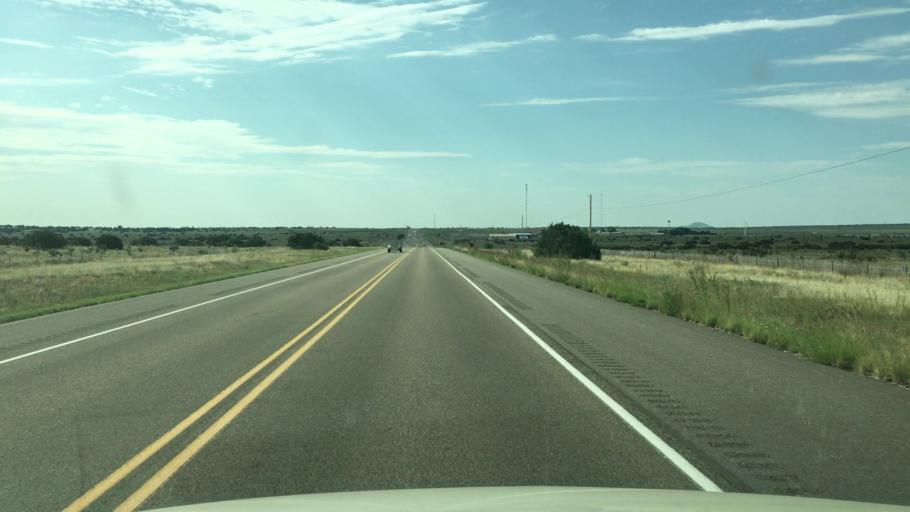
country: US
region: New Mexico
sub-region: Torrance County
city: Moriarty
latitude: 35.0247
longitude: -105.6735
